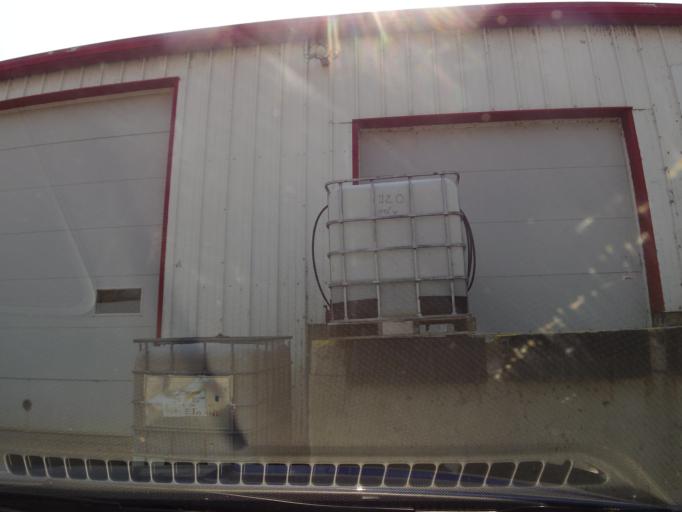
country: US
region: South Dakota
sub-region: Roberts County
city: Sisseton
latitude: 46.0776
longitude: -97.1526
